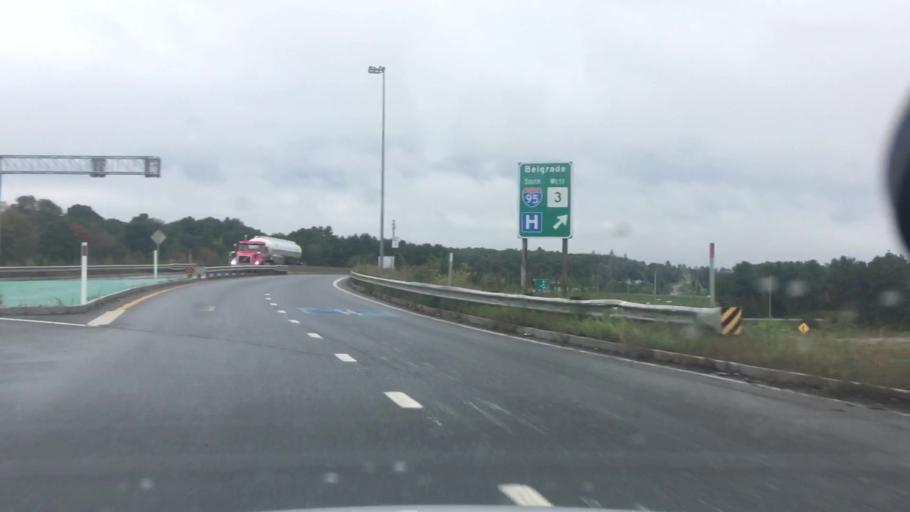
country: US
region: Maine
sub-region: Kennebec County
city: Augusta
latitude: 44.3537
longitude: -69.7807
